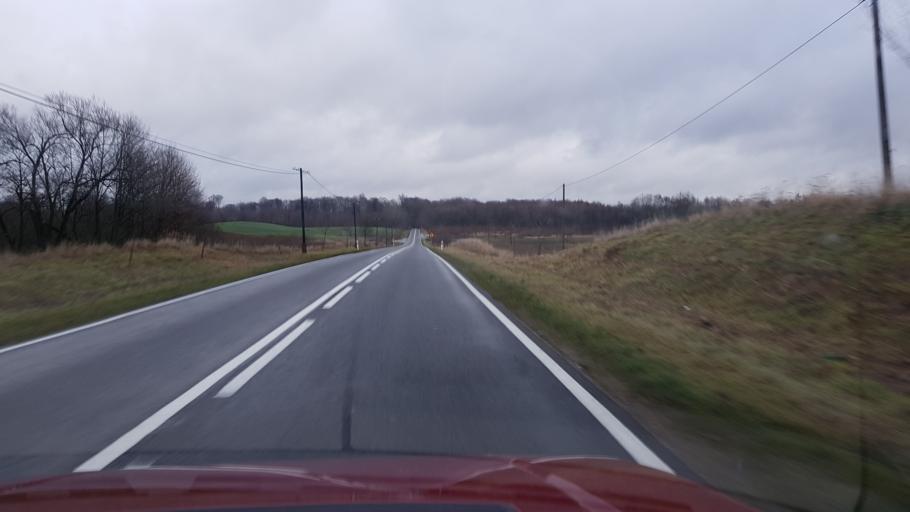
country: PL
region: West Pomeranian Voivodeship
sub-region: Powiat lobeski
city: Wegorzyno
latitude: 53.5257
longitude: 15.5870
